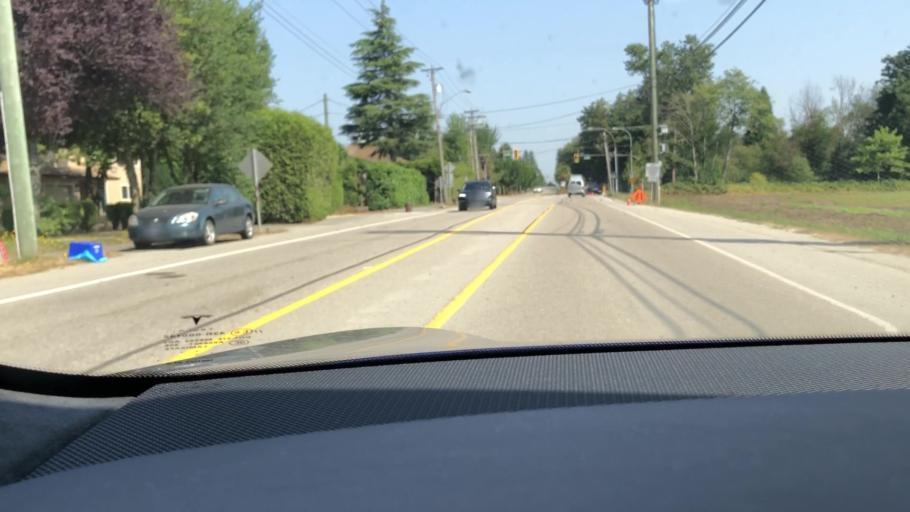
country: US
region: Washington
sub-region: Whatcom County
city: Point Roberts
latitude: 49.0127
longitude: -123.0686
